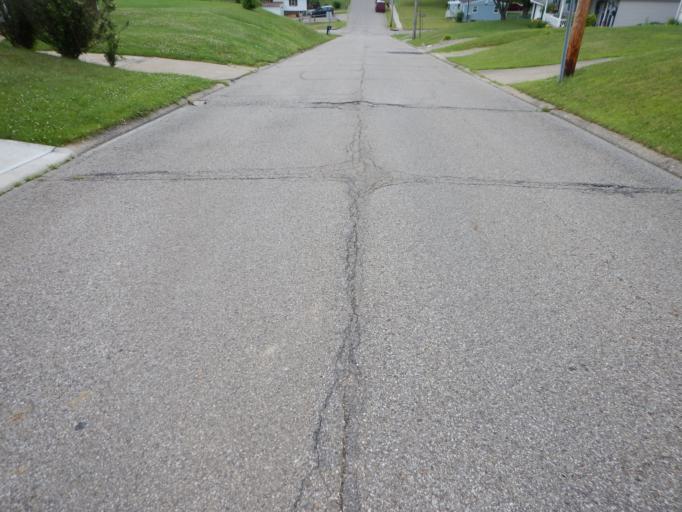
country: US
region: Ohio
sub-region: Muskingum County
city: South Zanesville
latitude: 39.9117
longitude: -82.0236
